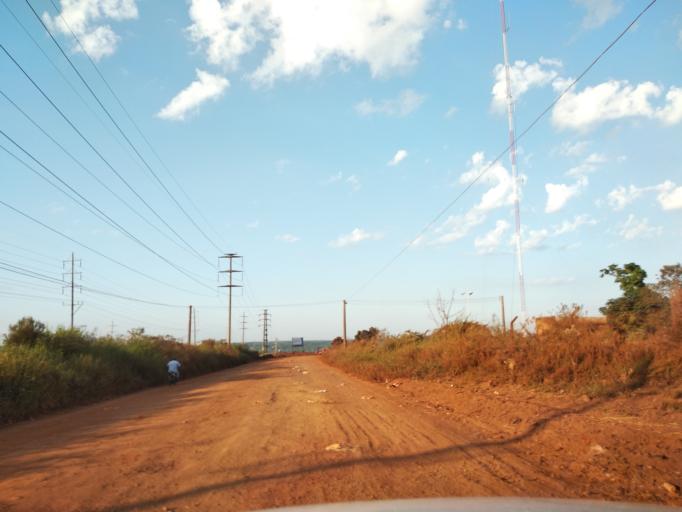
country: AR
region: Misiones
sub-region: Departamento de Capital
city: Posadas
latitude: -27.4438
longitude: -55.9165
